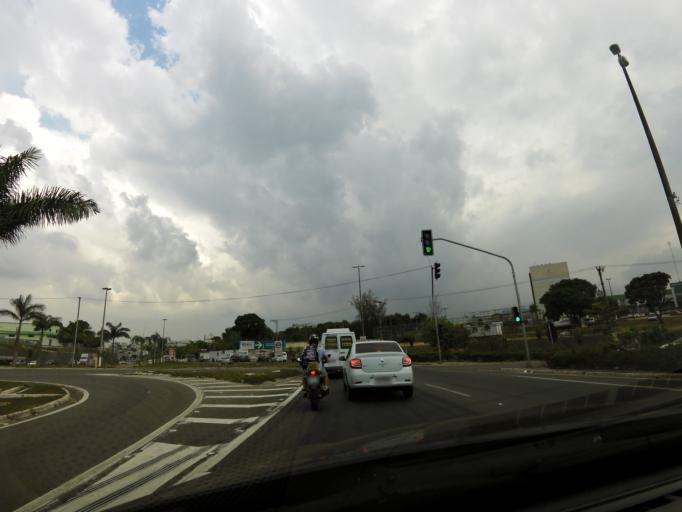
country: BR
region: Espirito Santo
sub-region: Vitoria
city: Vitoria
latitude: -20.3353
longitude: -40.3762
